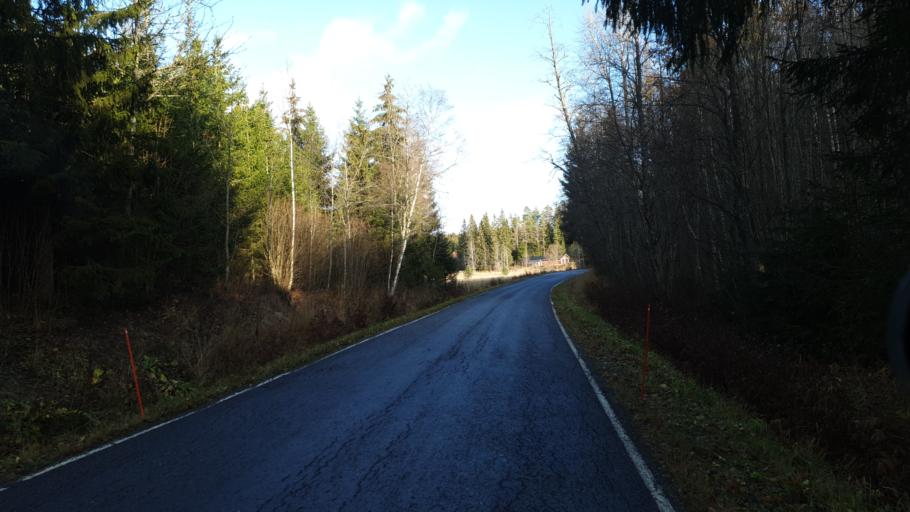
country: FI
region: Uusimaa
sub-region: Helsinki
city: Siuntio
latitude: 60.2049
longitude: 24.2345
